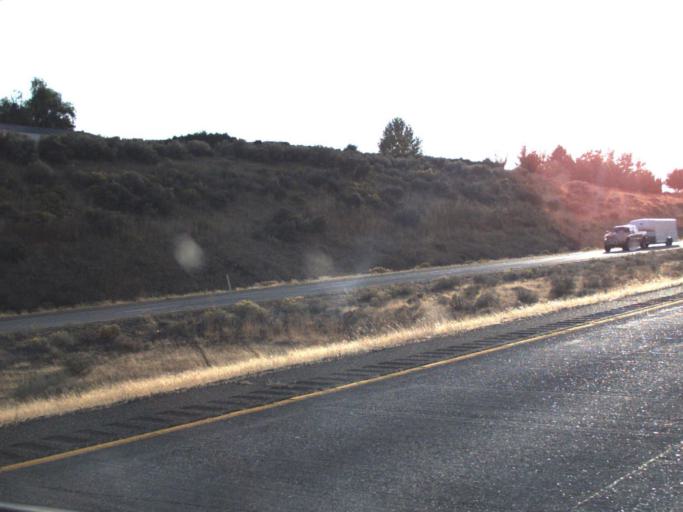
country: US
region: Washington
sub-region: Benton County
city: Richland
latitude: 46.1979
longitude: -119.2980
